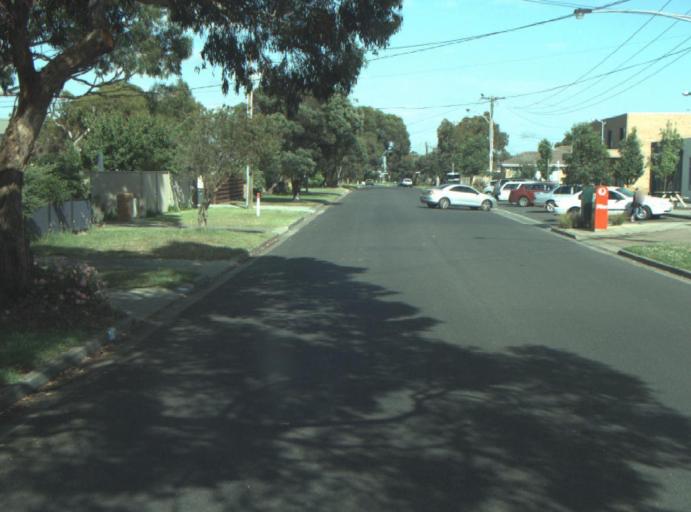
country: AU
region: Victoria
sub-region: Greater Geelong
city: Leopold
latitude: -38.2834
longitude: 144.5216
